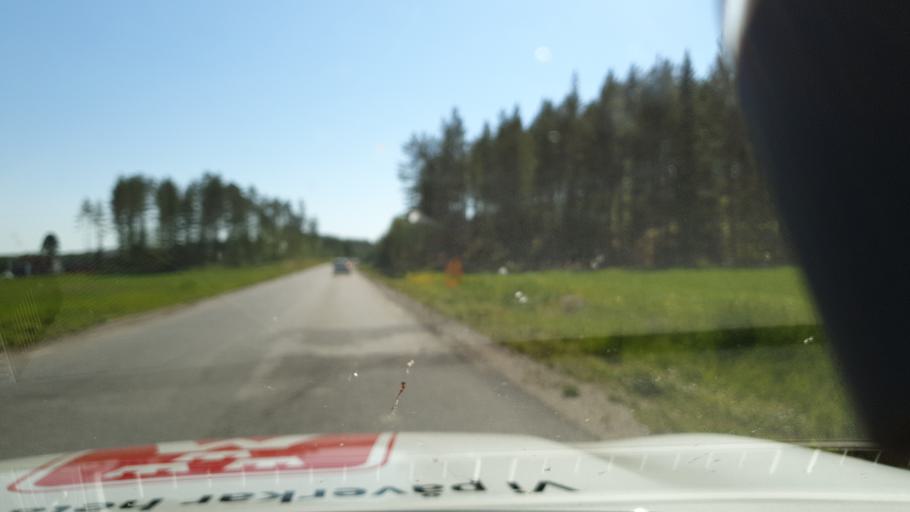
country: SE
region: Vaesterbotten
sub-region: Vindelns Kommun
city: Vindeln
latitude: 64.2458
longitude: 19.8344
